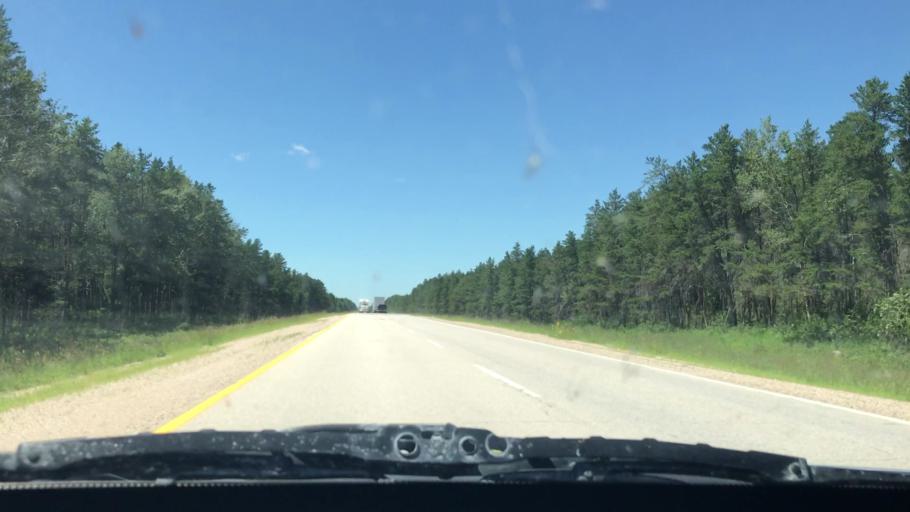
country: CA
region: Manitoba
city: La Broquerie
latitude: 49.6566
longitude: -96.1795
